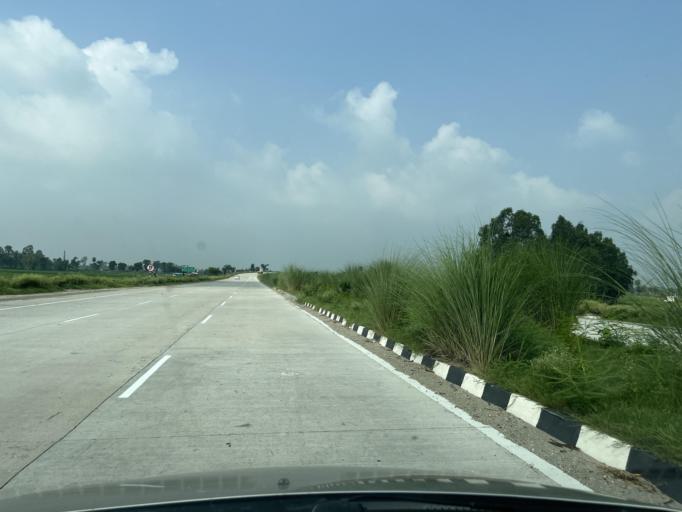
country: IN
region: Uttarakhand
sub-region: Udham Singh Nagar
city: Kashipur
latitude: 29.1643
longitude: 78.9701
